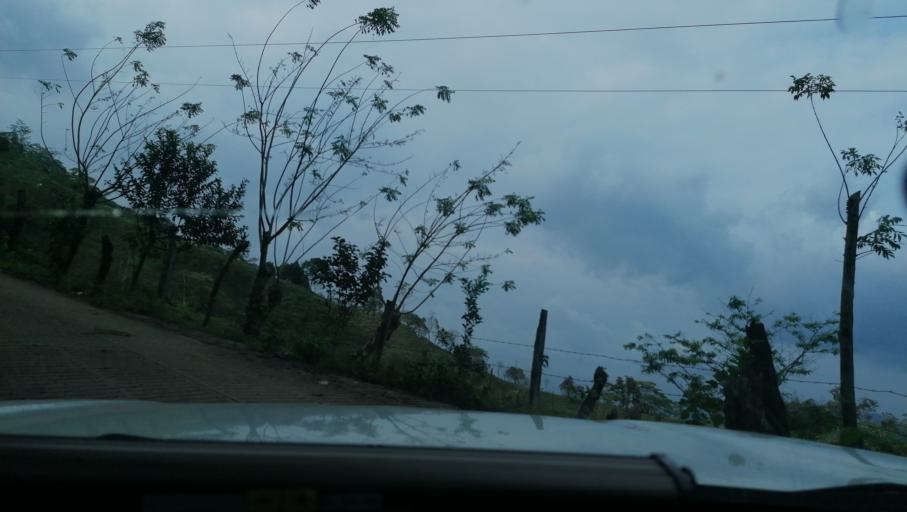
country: MX
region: Chiapas
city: Ixtacomitan
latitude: 17.3341
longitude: -93.1071
